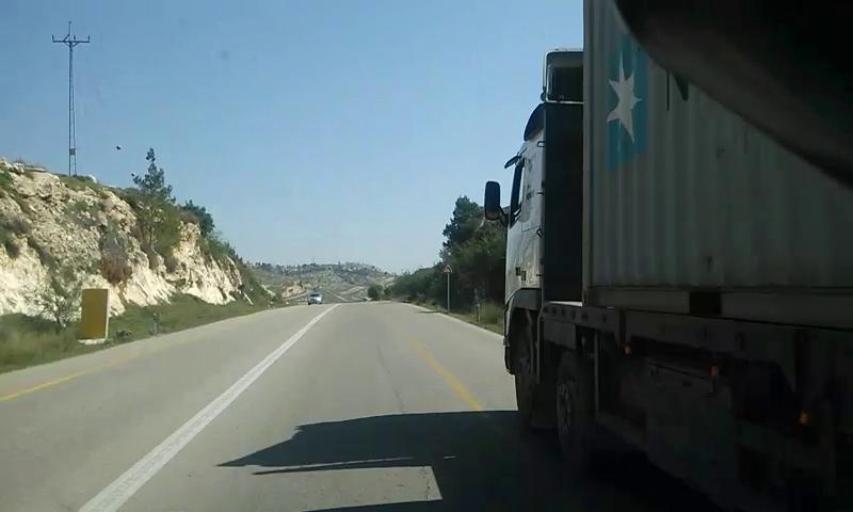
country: PS
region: West Bank
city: Tarqumya
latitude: 31.5607
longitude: 35.0052
